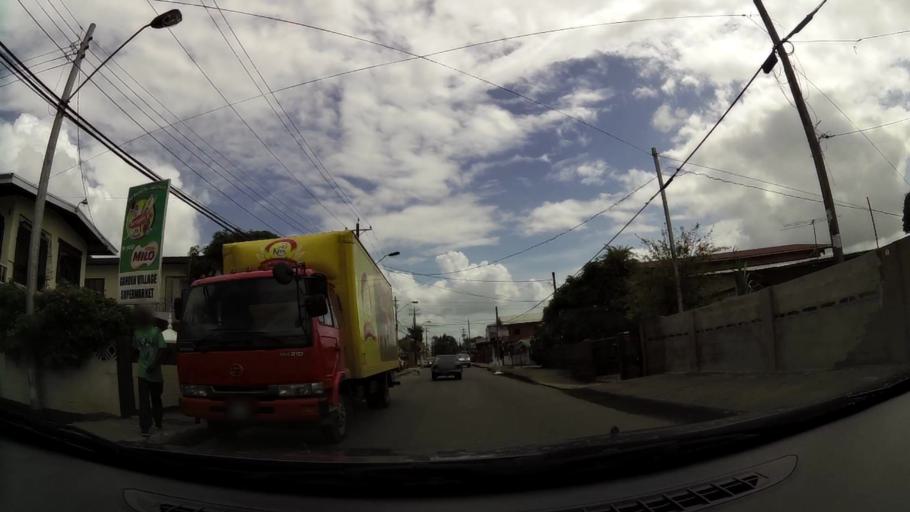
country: TT
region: Tunapuna/Piarco
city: Arouca
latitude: 10.6319
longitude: -61.3244
